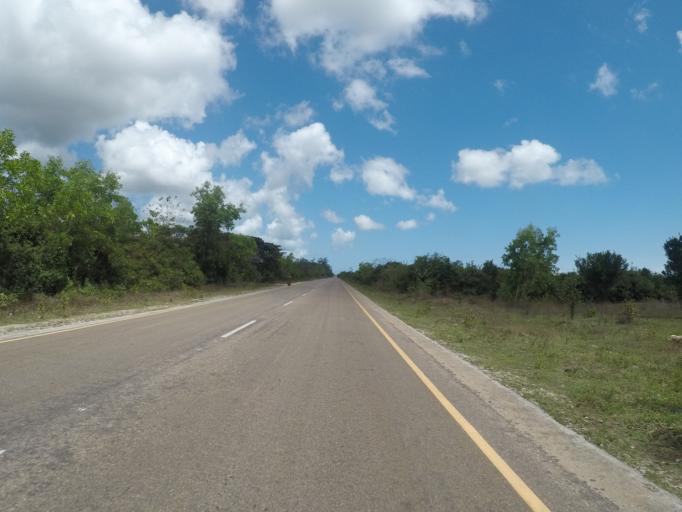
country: TZ
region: Zanzibar Central/South
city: Koani
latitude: -6.2520
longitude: 39.3556
